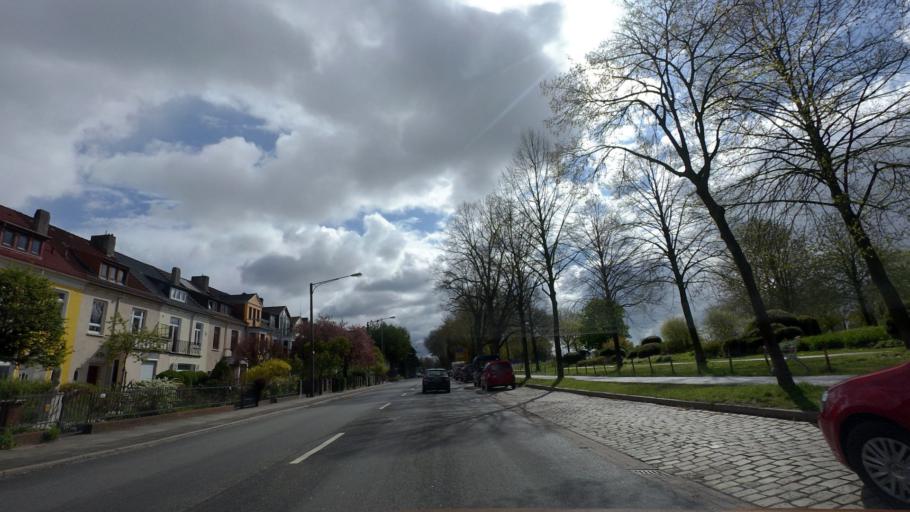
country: DE
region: Bremen
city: Bremen
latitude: 53.0631
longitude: 8.8621
